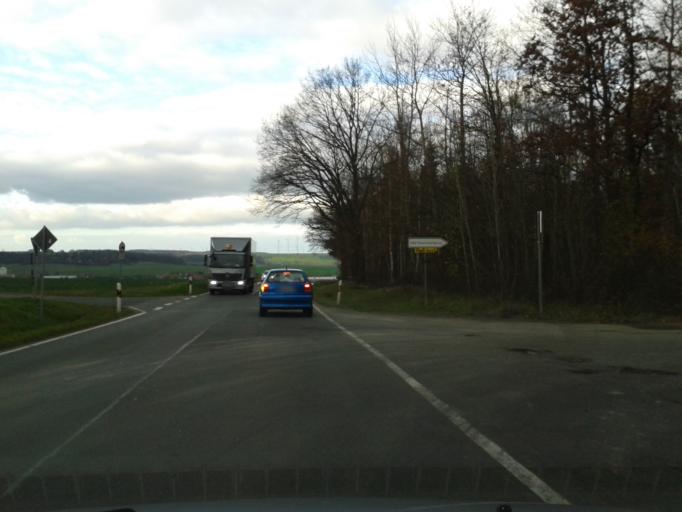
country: DE
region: Thuringia
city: Hainspitz
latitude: 50.9429
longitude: 11.8261
